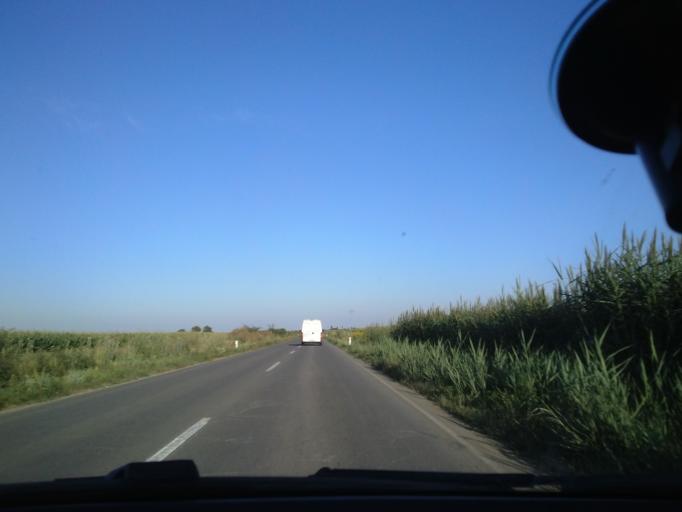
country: RS
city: Despotovo
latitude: 45.4055
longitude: 19.4273
